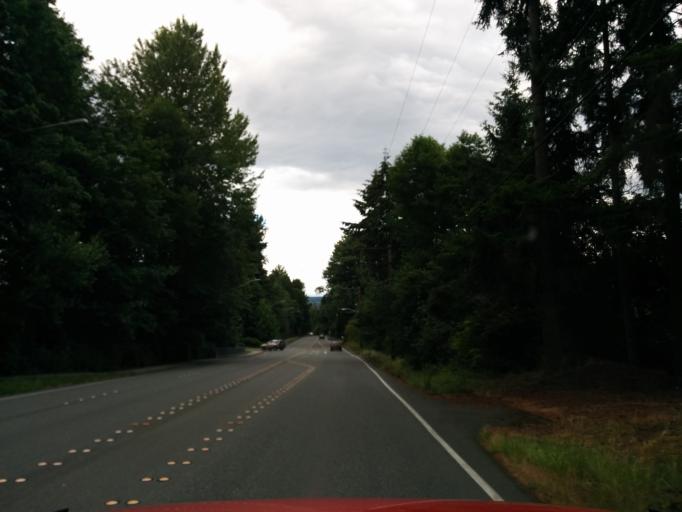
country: US
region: Washington
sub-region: King County
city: Redmond
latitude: 47.6409
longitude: -122.1195
